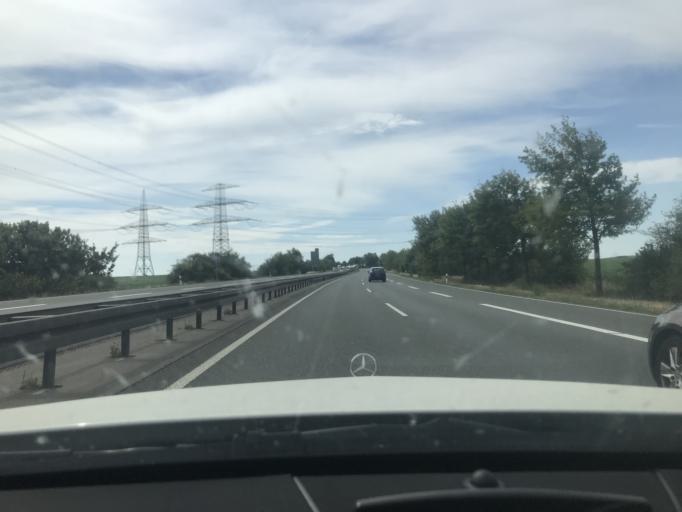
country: DE
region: Thuringia
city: Monchenholzhausen
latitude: 50.9689
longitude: 11.1383
